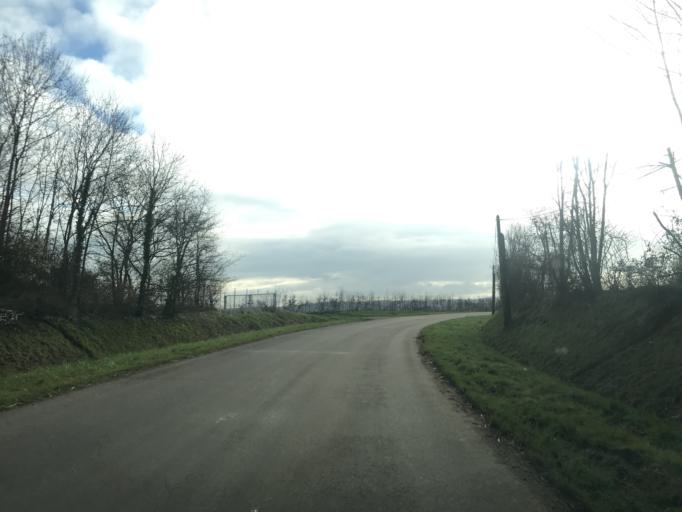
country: FR
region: Lower Normandy
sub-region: Departement du Calvados
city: Dives-sur-Mer
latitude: 49.2218
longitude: -0.1069
